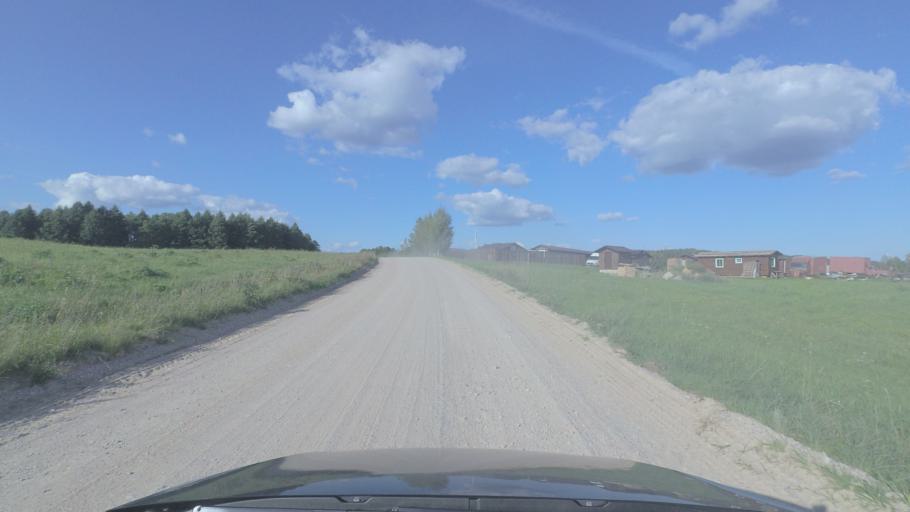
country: LT
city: Pabrade
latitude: 55.1360
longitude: 25.7090
